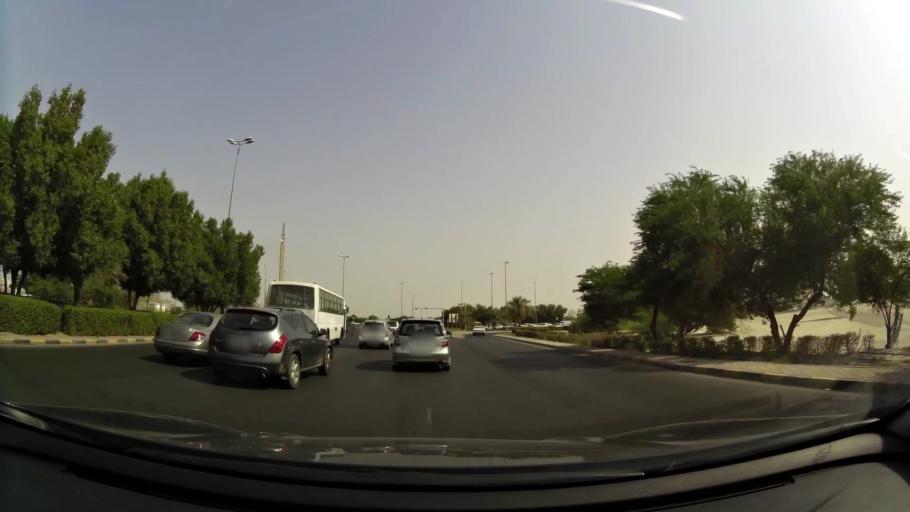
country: KW
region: Muhafazat al Jahra'
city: Al Jahra'
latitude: 29.3361
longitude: 47.6649
